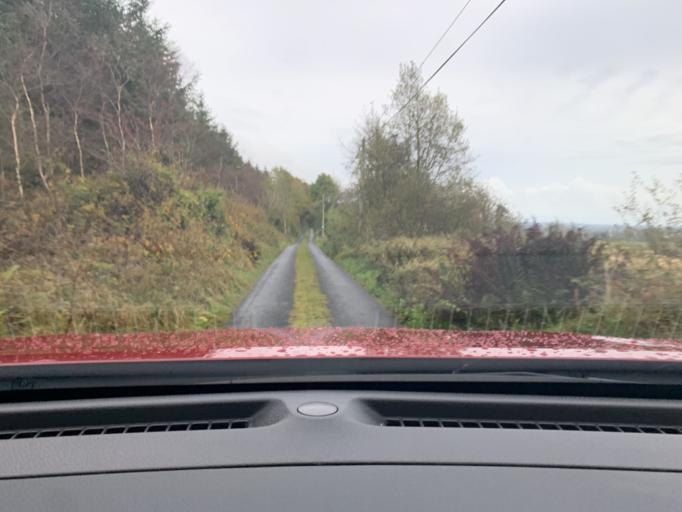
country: IE
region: Connaught
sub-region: Roscommon
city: Ballaghaderreen
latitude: 53.9187
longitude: -8.5574
